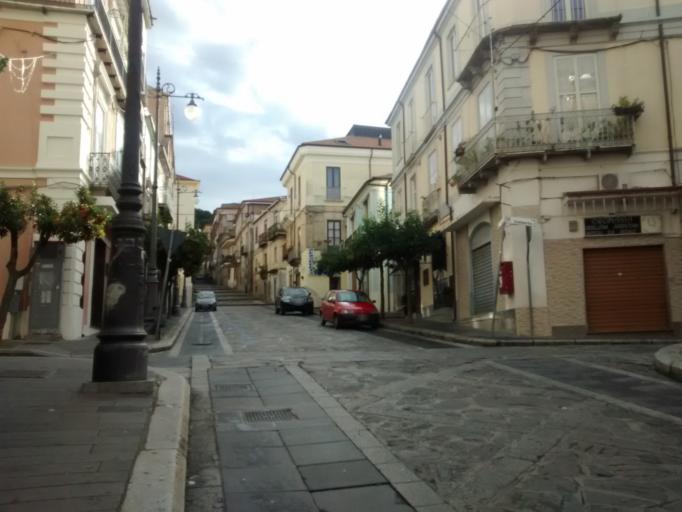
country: IT
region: Calabria
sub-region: Provincia di Vibo-Valentia
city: Vibo Valentia
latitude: 38.6726
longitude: 16.1046
